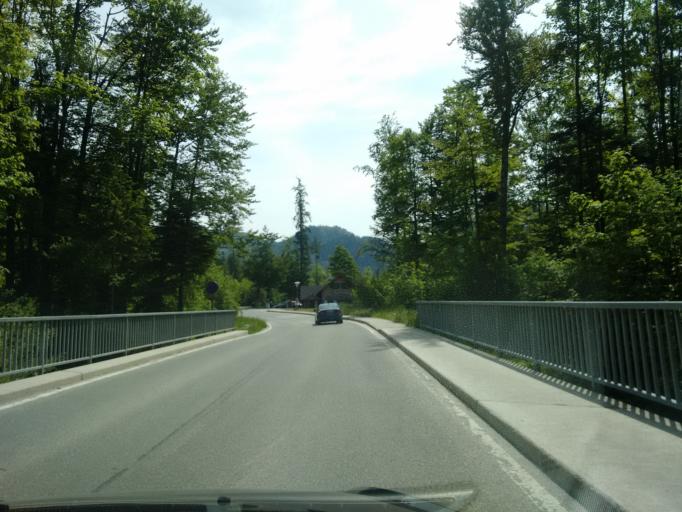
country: AT
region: Styria
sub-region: Politischer Bezirk Liezen
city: Bad Aussee
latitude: 47.6390
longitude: 13.8827
